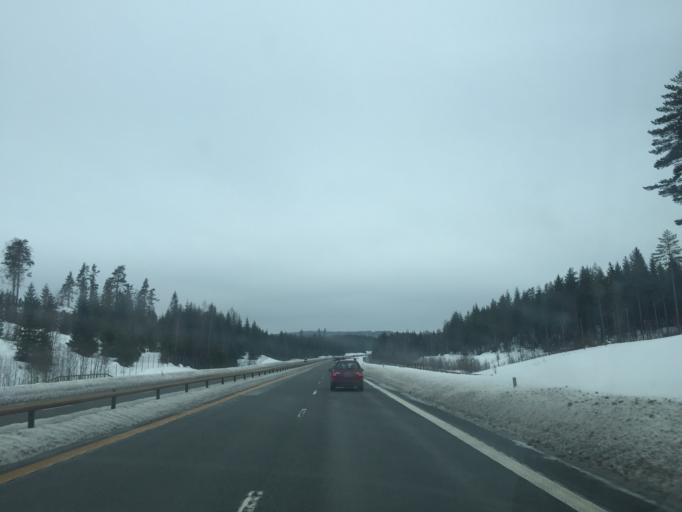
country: NO
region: Hedmark
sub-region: Stange
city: Stange
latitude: 60.6124
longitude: 11.3057
